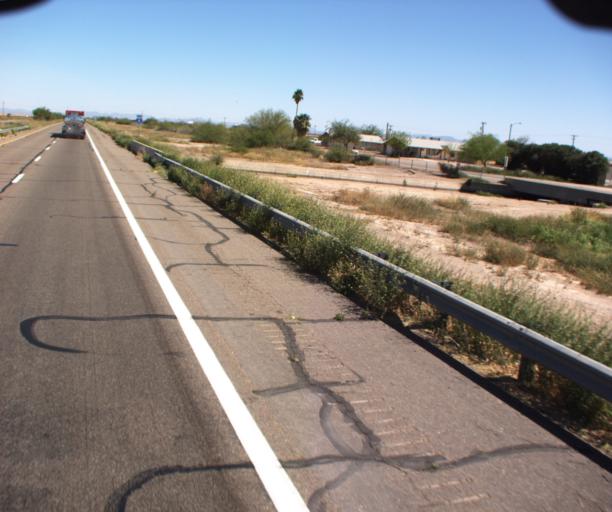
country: US
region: Arizona
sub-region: Maricopa County
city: Gila Bend
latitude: 32.9228
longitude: -112.8792
